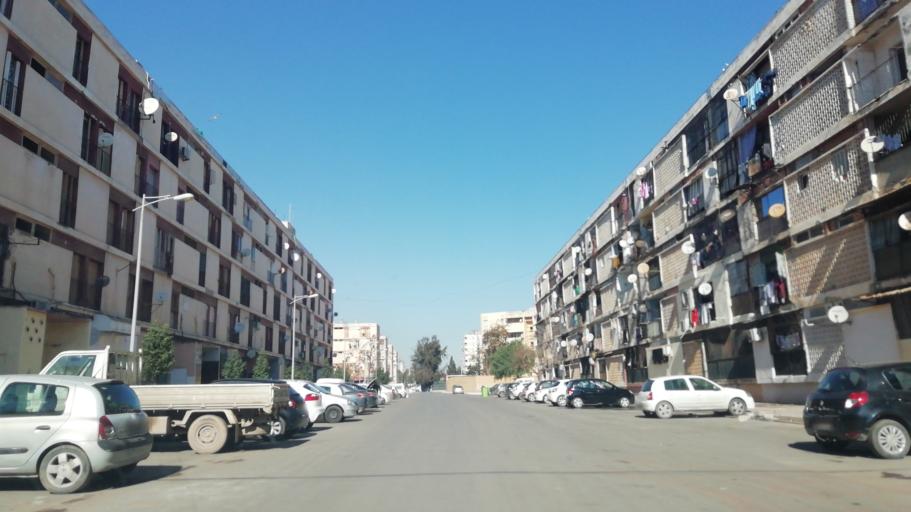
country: DZ
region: Oran
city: Oran
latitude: 35.6779
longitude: -0.6379
